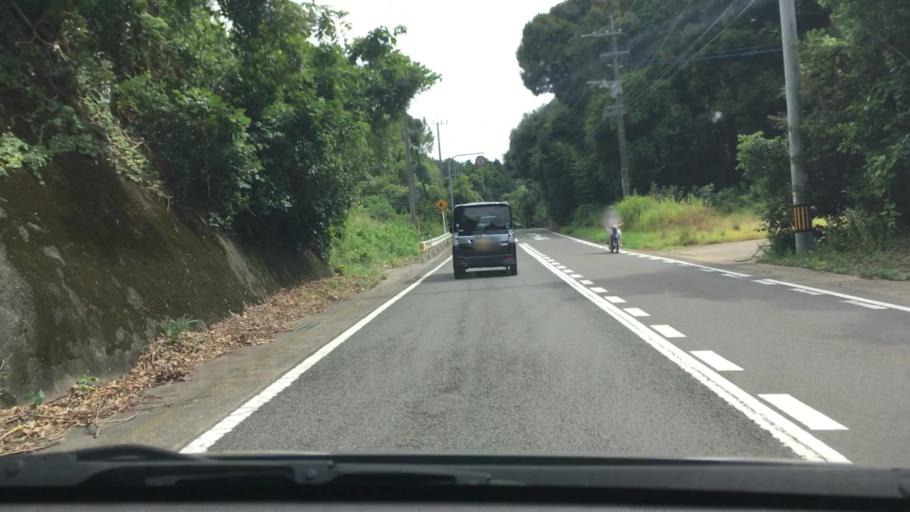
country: JP
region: Nagasaki
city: Togitsu
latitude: 32.9217
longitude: 129.7877
